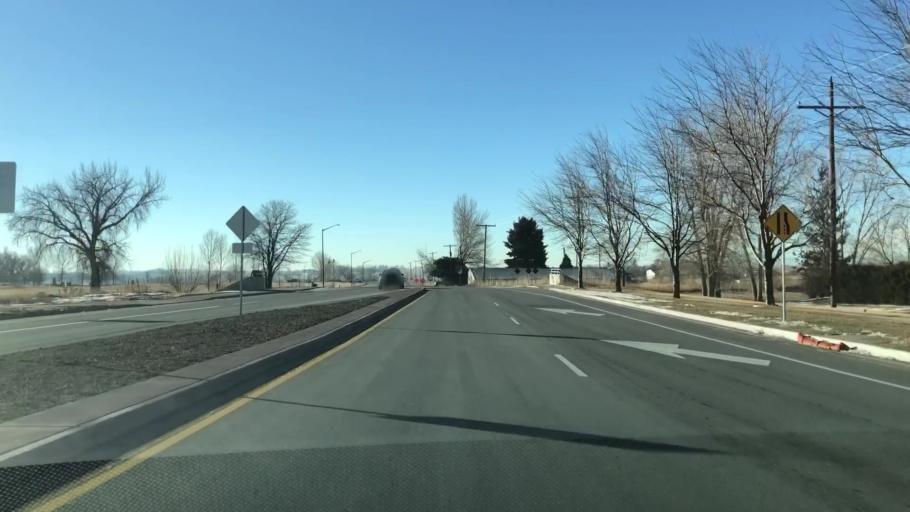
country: US
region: Colorado
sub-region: Larimer County
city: Loveland
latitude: 40.4046
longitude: -105.0211
